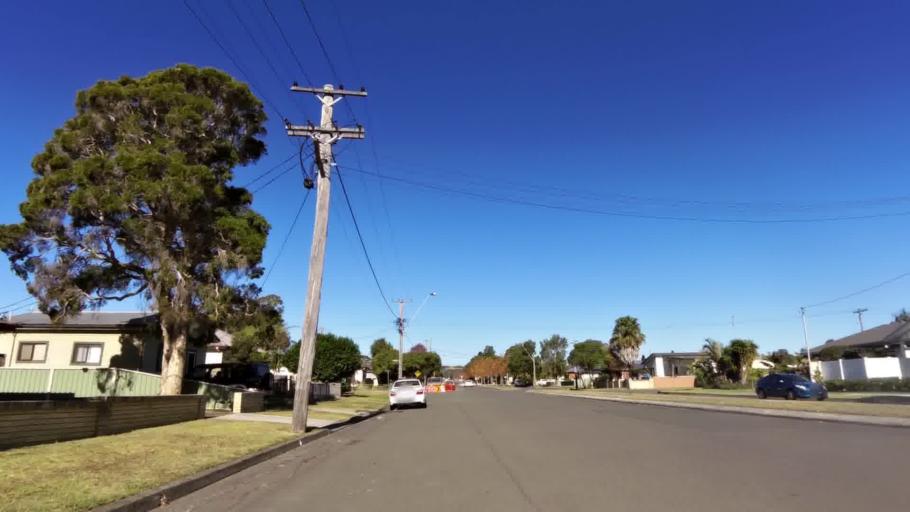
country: AU
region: New South Wales
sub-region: Shellharbour
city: Albion Park Rail
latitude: -34.5574
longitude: 150.8184
